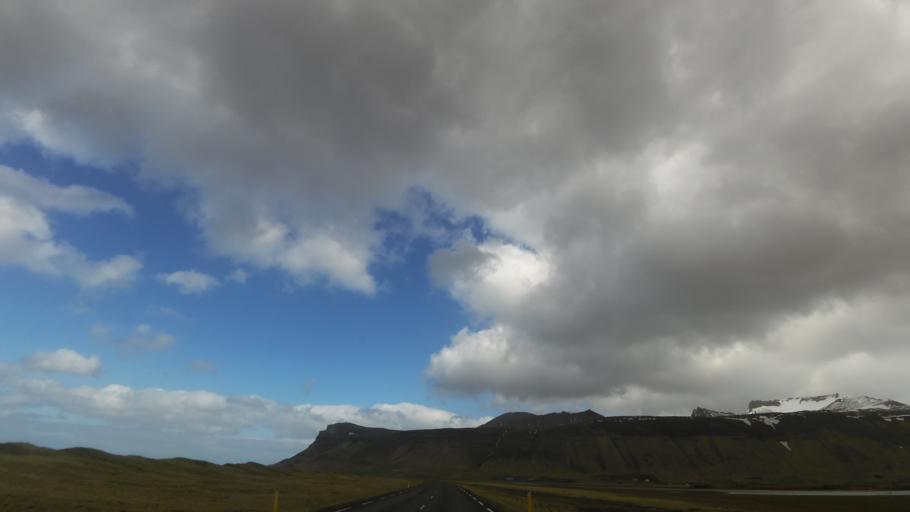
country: IS
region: West
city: Olafsvik
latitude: 64.9208
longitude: -23.5260
